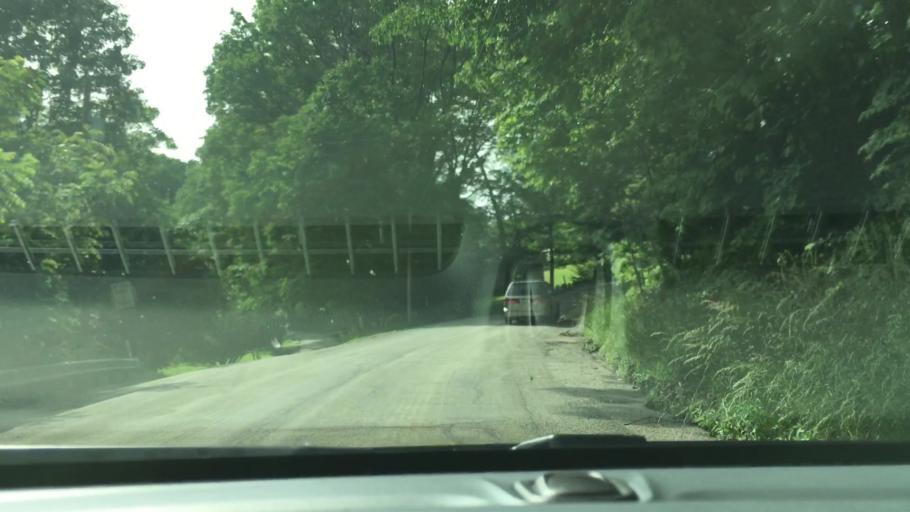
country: US
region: Pennsylvania
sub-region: Westmoreland County
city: New Stanton
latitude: 40.2599
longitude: -79.6170
